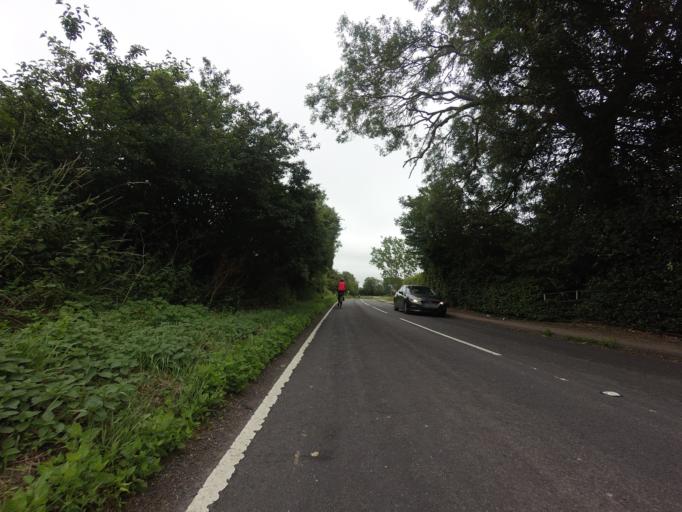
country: GB
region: England
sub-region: Kent
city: Meopham
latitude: 51.3795
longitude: 0.3525
